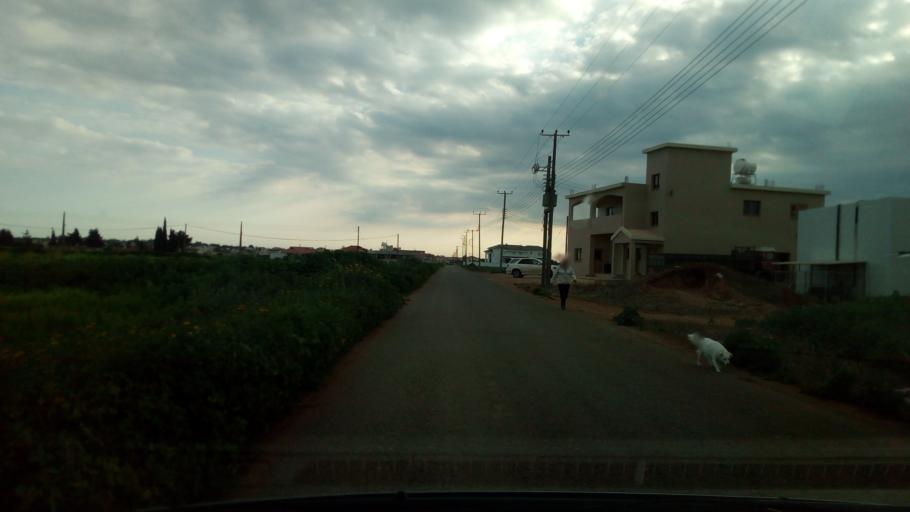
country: CY
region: Ammochostos
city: Avgorou
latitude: 34.9834
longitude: 33.8447
